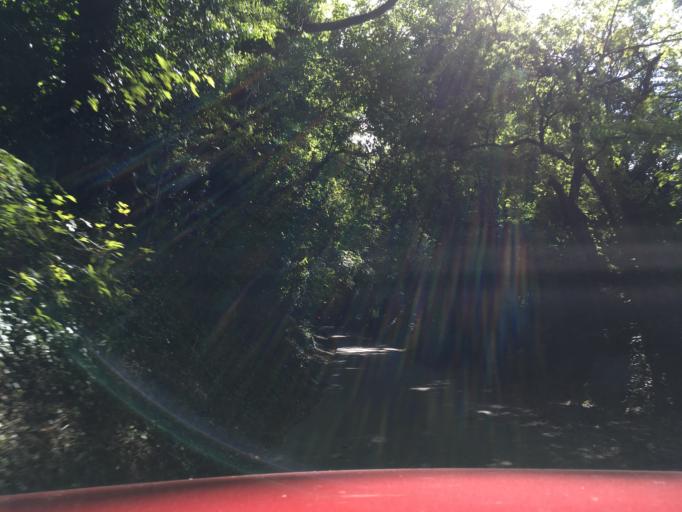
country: GB
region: England
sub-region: Wiltshire
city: Erlestoke
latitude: 51.2785
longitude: -2.0657
